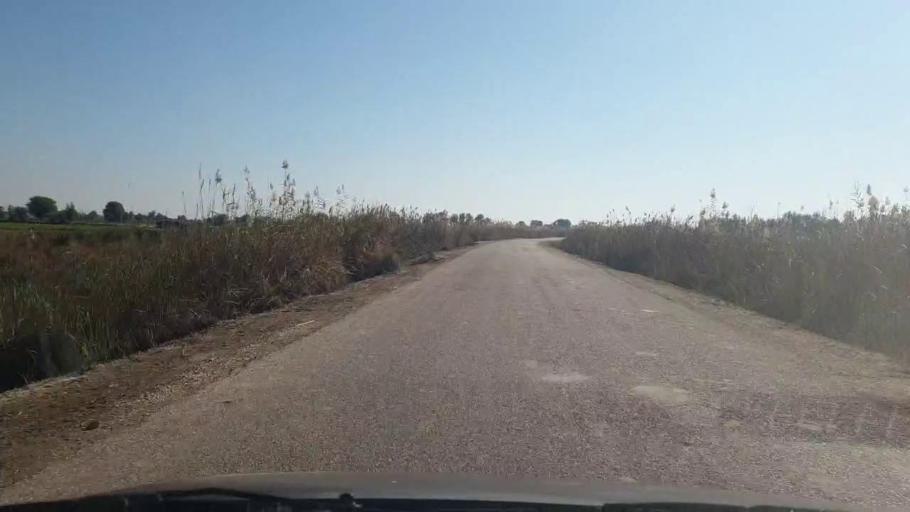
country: PK
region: Sindh
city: Bozdar
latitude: 27.1573
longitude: 68.6514
